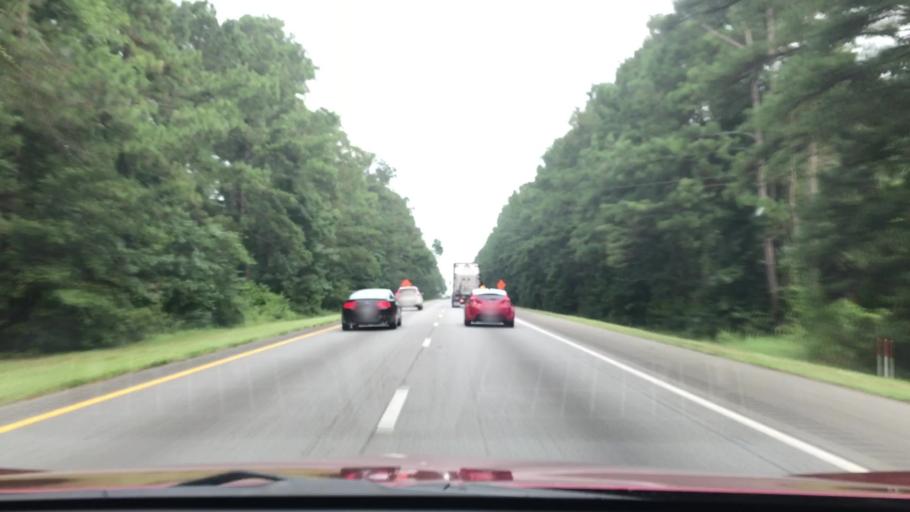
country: US
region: South Carolina
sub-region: Dorchester County
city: Ridgeville
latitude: 33.1045
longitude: -80.2487
